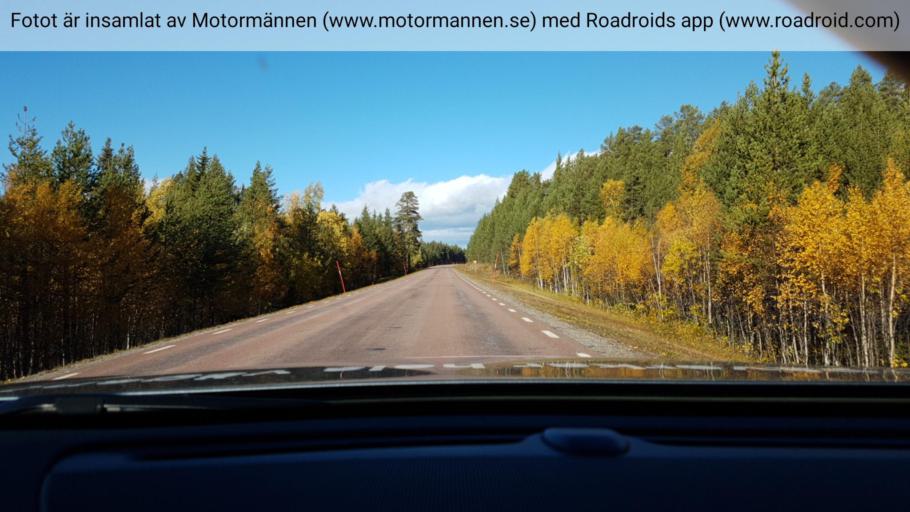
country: SE
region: Norrbotten
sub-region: Arjeplogs Kommun
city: Arjeplog
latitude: 66.0163
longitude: 18.0802
